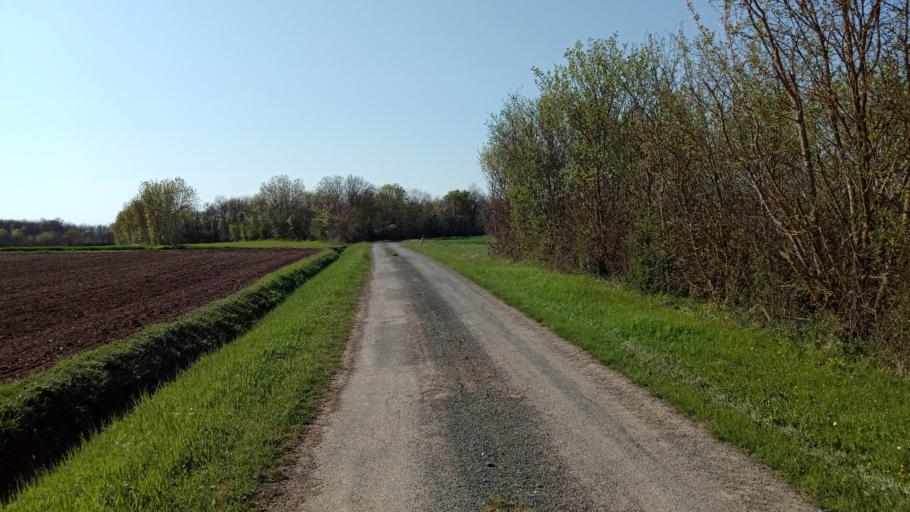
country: FR
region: Poitou-Charentes
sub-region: Departement de la Charente-Maritime
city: Verines
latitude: 46.1608
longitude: -0.9362
